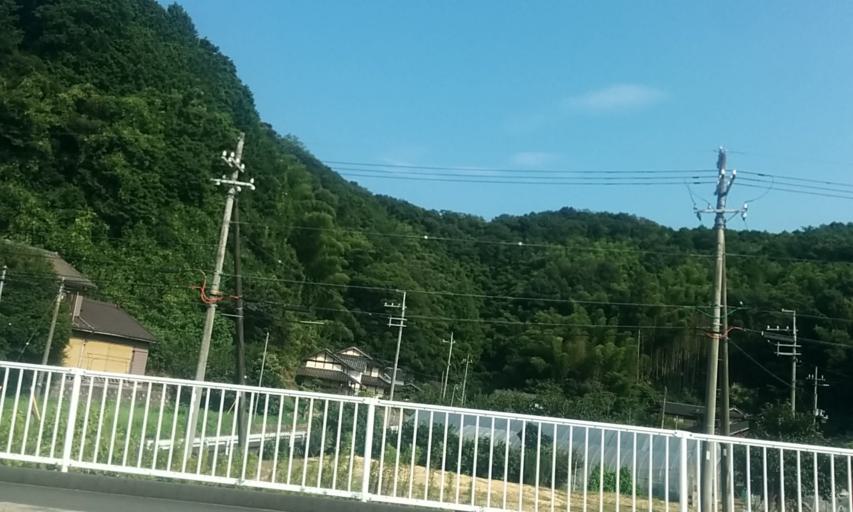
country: JP
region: Kyoto
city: Maizuru
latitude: 35.4534
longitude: 135.2718
